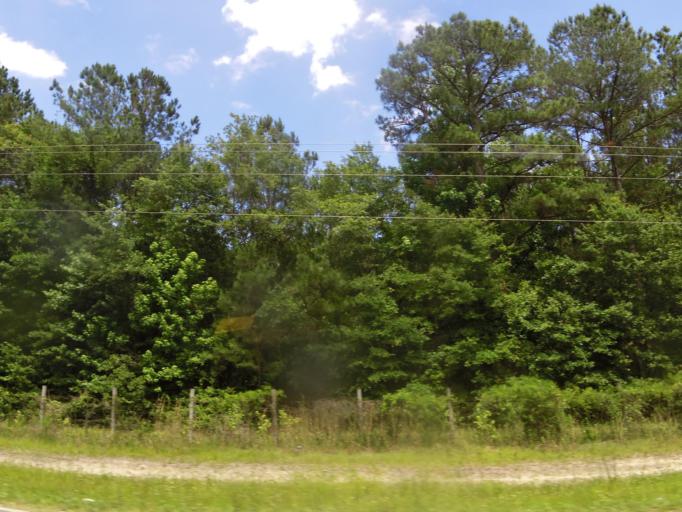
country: US
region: Florida
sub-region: Clay County
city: Green Cove Springs
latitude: 29.9922
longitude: -81.7313
